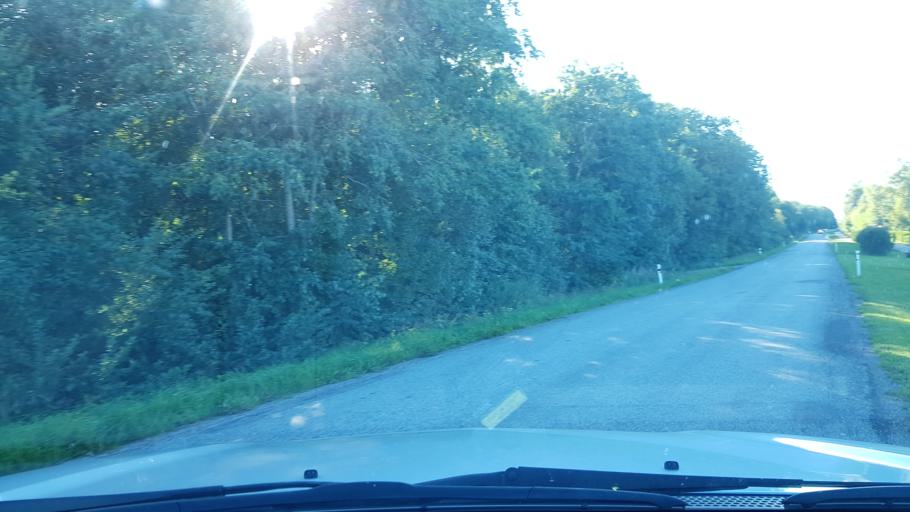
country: EE
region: Harju
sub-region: Rae vald
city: Jueri
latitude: 59.3835
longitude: 24.8687
